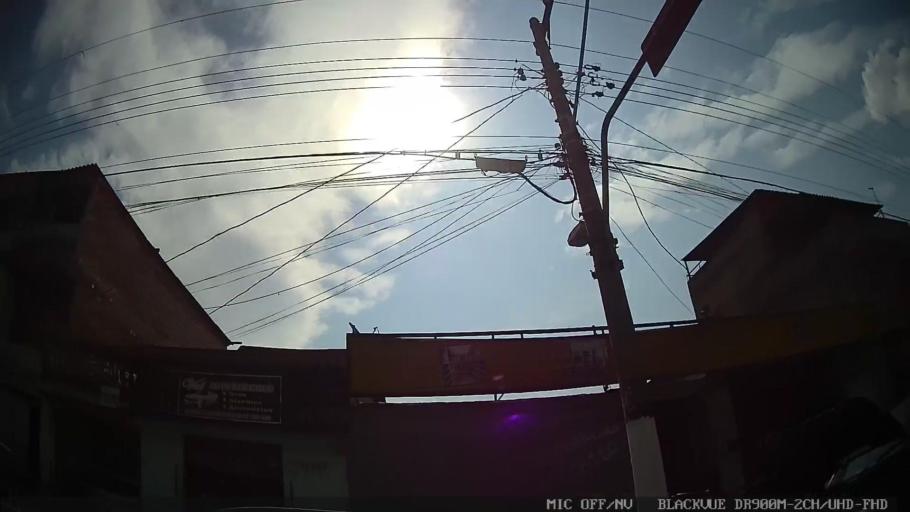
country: BR
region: Sao Paulo
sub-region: Itaquaquecetuba
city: Itaquaquecetuba
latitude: -23.4860
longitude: -46.4152
